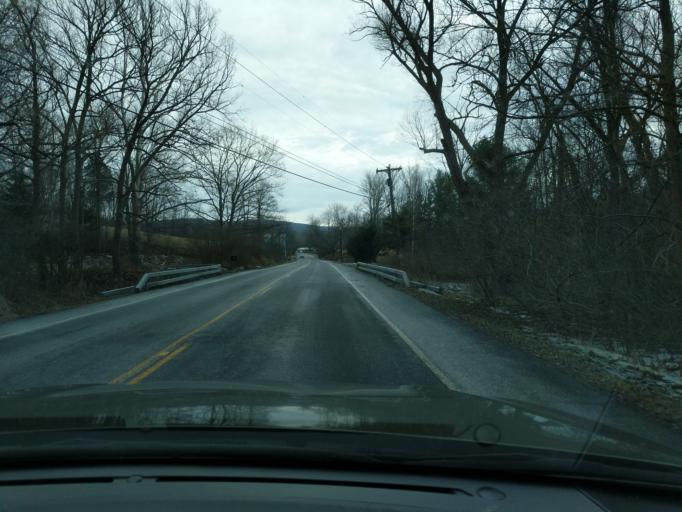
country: US
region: New York
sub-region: Tompkins County
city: East Ithaca
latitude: 42.3941
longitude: -76.4183
